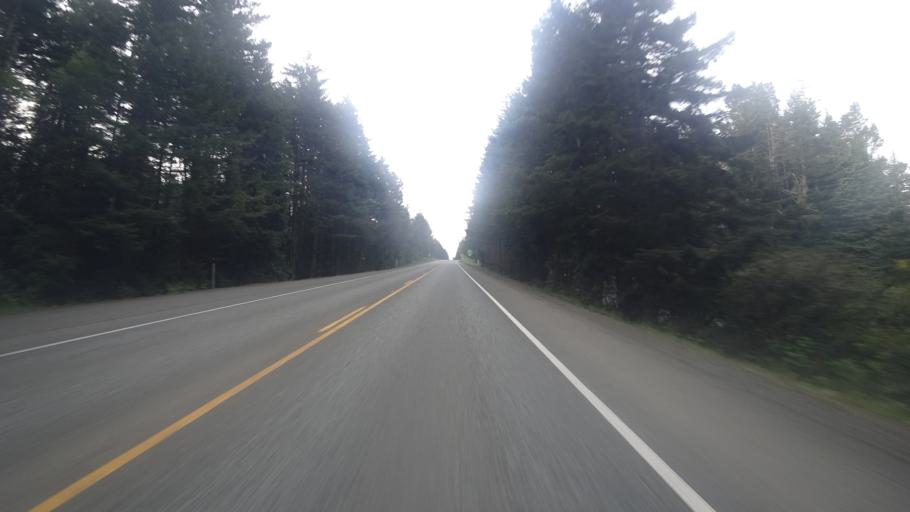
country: US
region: Oregon
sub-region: Coos County
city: Lakeside
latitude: 43.5262
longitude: -124.2162
